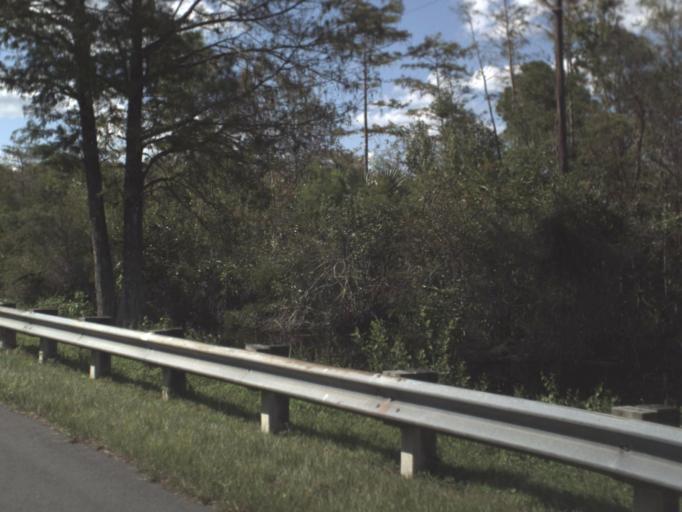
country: US
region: Florida
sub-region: Collier County
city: Marco
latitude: 25.8764
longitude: -81.2250
